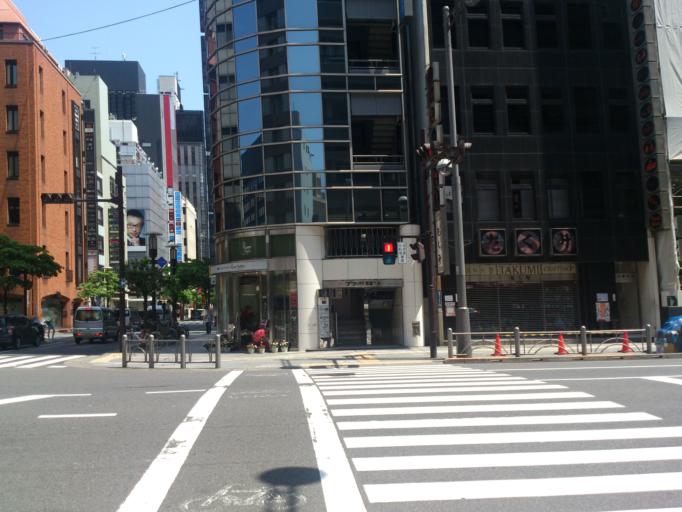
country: JP
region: Tokyo
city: Tokyo
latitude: 35.6698
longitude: 139.7604
